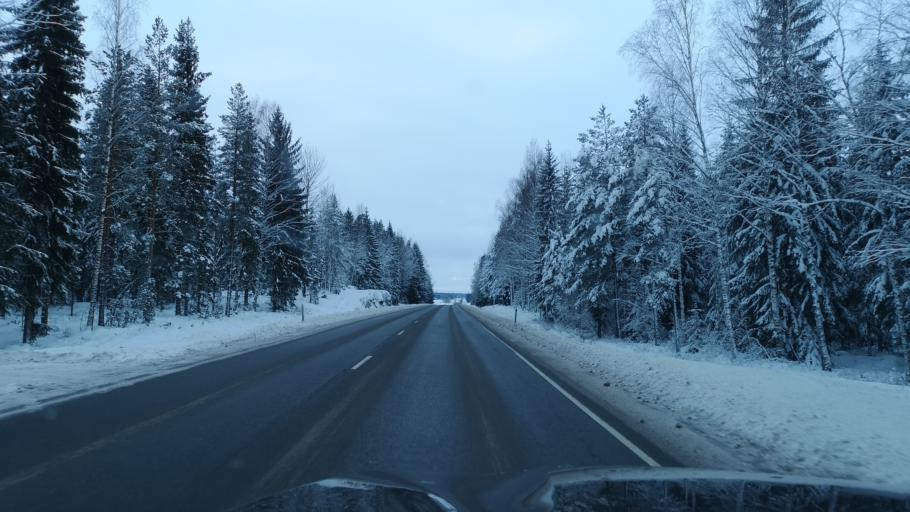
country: FI
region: Varsinais-Suomi
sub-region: Loimaa
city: Loimaa
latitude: 60.9003
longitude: 23.1366
